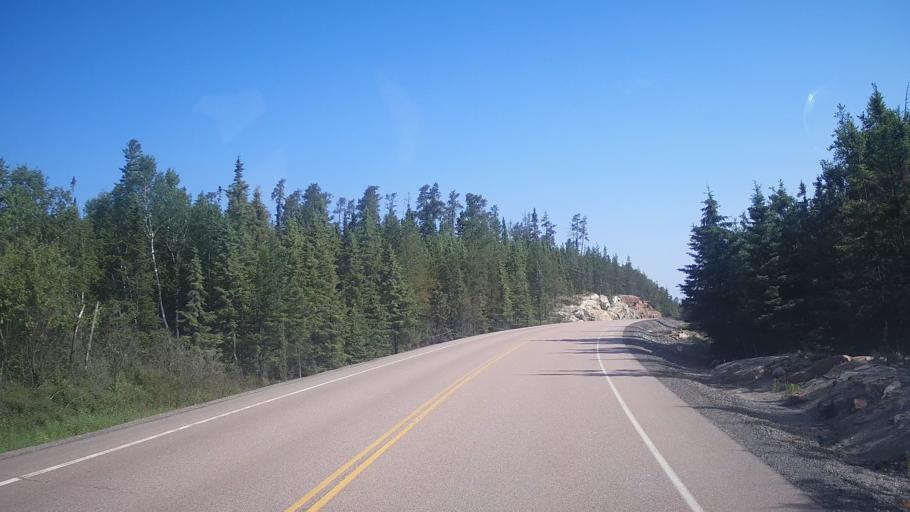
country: CA
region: Ontario
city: Rayside-Balfour
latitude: 46.9826
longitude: -81.6346
